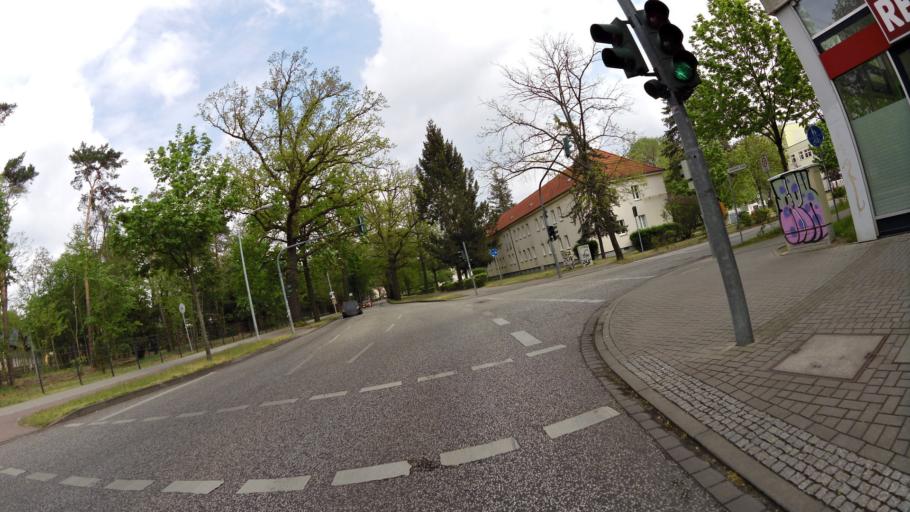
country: DE
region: Brandenburg
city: Konigs Wusterhausen
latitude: 52.2890
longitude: 13.6171
